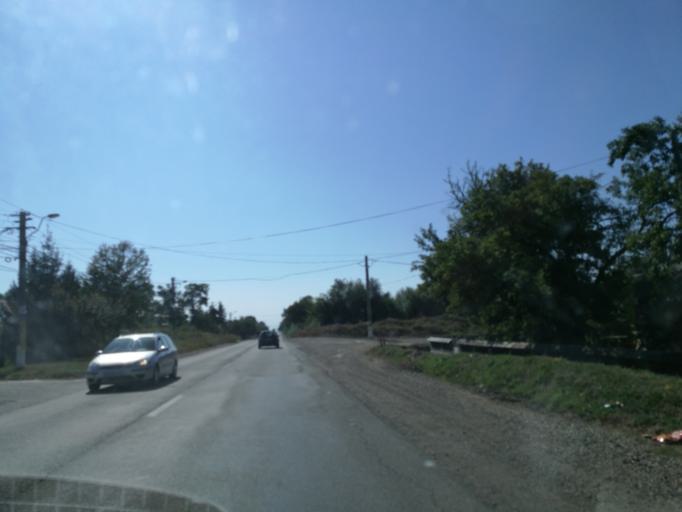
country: RO
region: Iasi
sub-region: Comuna Miroslavesti
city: Miroslavesti
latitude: 47.1512
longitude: 26.6420
